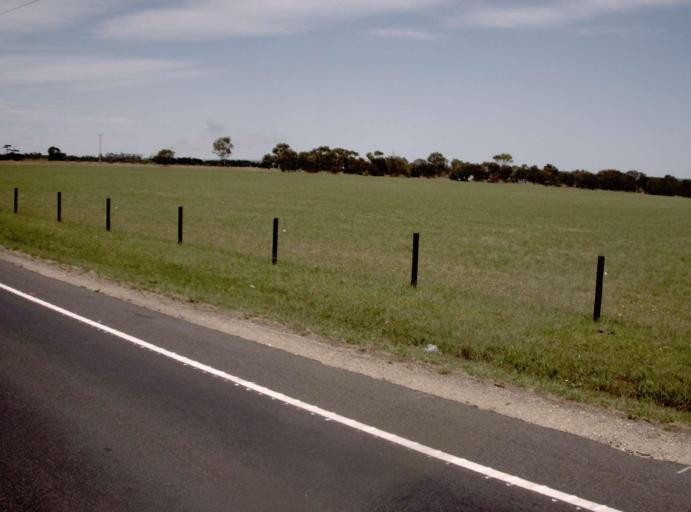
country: AU
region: Victoria
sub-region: Wellington
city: Sale
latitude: -38.1005
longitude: 146.9613
